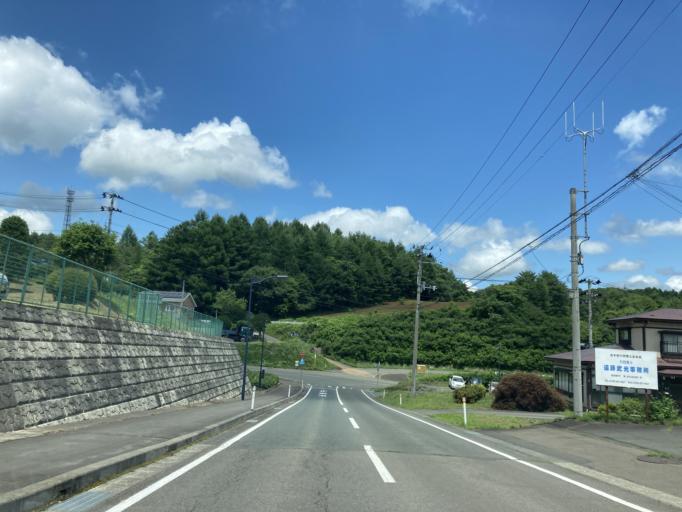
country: JP
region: Iwate
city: Ichinohe
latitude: 39.9726
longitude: 141.2132
